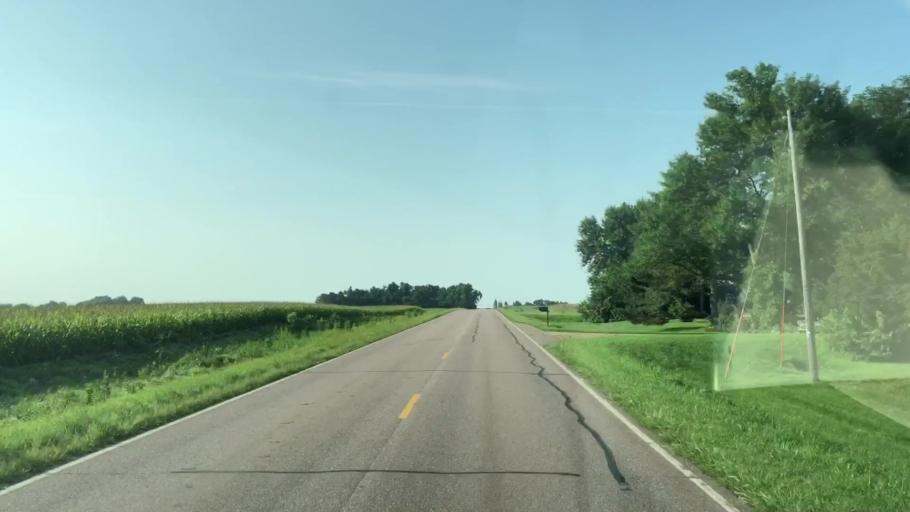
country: US
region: Iowa
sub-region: Lyon County
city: George
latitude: 43.2402
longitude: -96.0005
